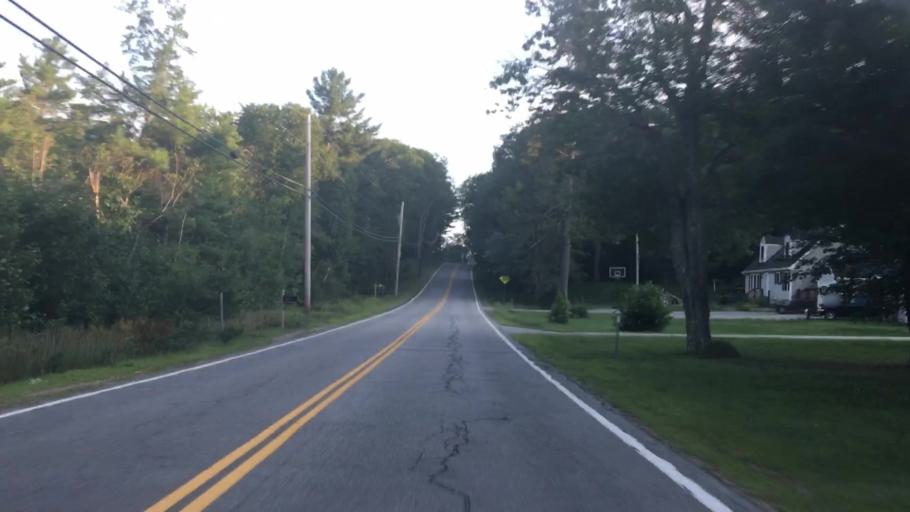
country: US
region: New Hampshire
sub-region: Belknap County
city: Gilmanton
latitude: 43.4332
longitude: -71.4161
